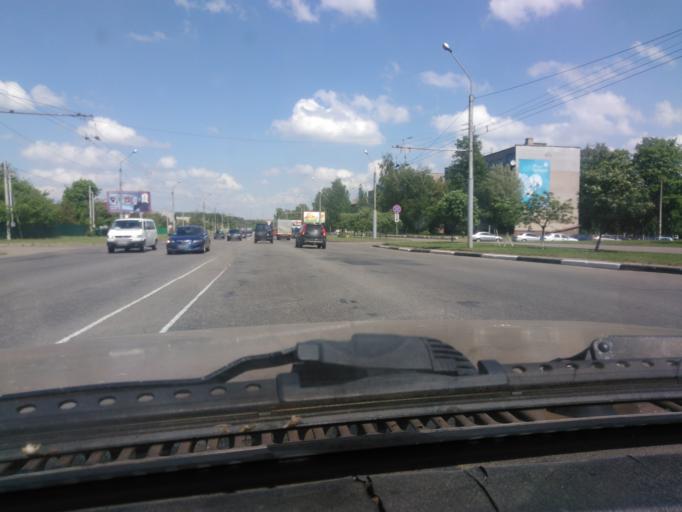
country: BY
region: Mogilev
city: Mahilyow
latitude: 53.9387
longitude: 30.3540
